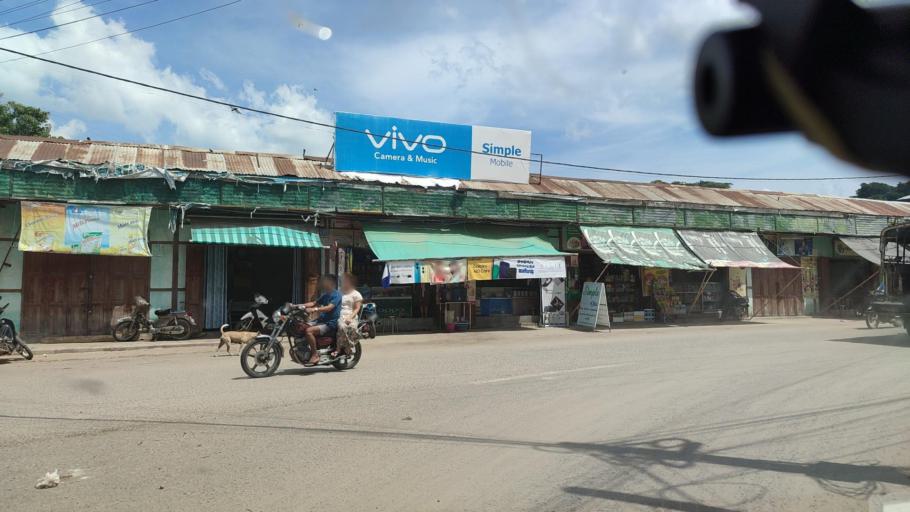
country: MM
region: Magway
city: Pakokku
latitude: 21.2007
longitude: 94.9082
